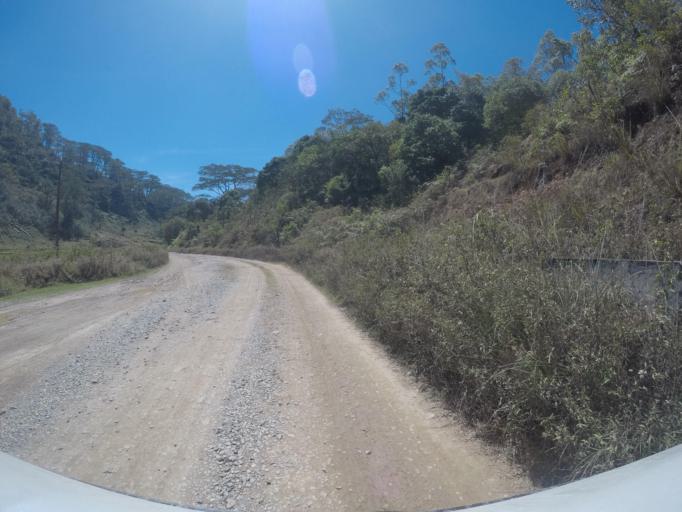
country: TL
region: Ermera
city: Gleno
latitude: -8.7755
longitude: 125.3926
